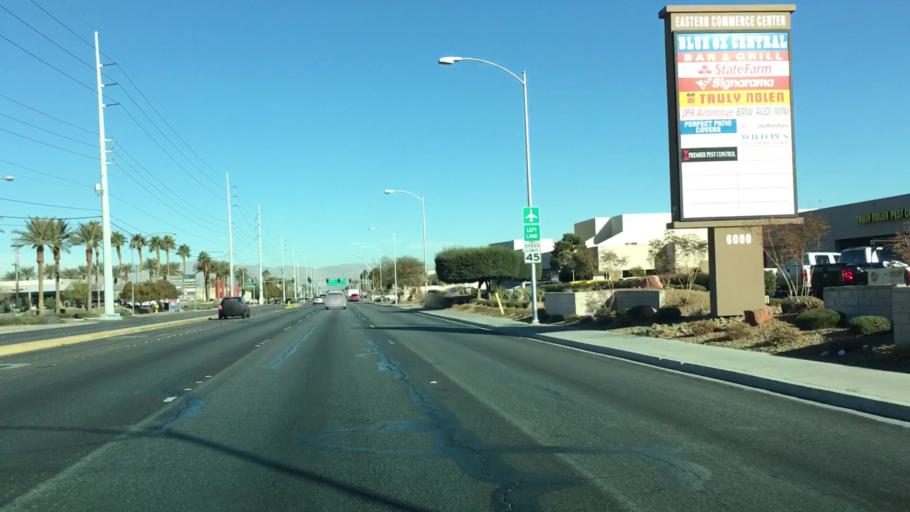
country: US
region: Nevada
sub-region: Clark County
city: Paradise
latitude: 36.0802
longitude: -115.1186
